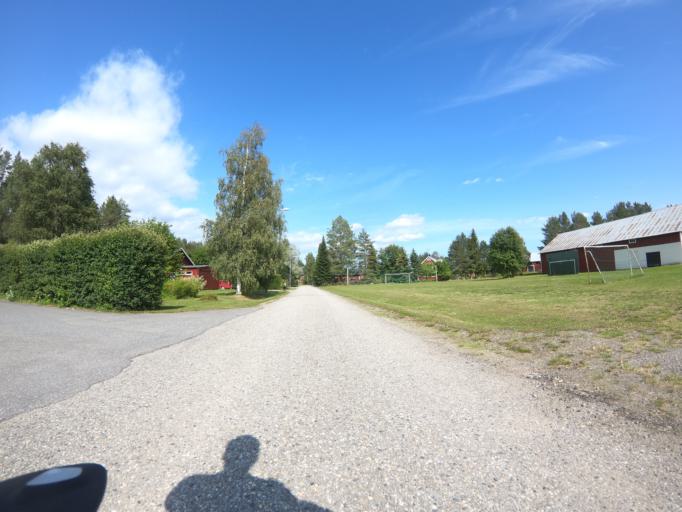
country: SE
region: Vaesterbotten
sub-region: Umea Kommun
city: Roback
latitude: 63.8315
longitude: 20.1143
